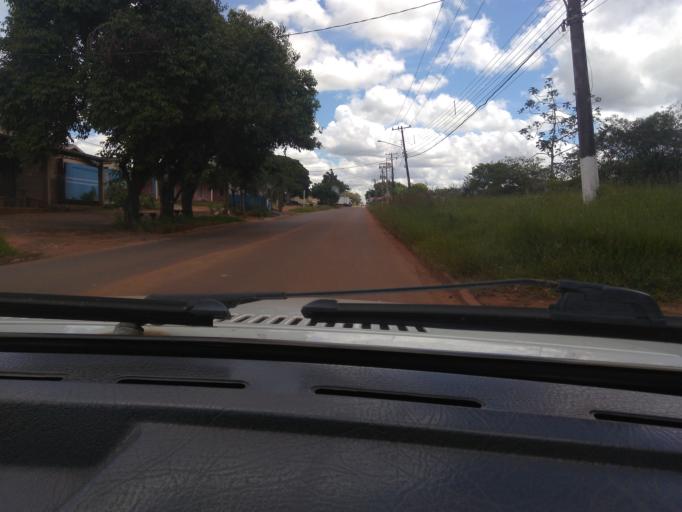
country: BR
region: Mato Grosso do Sul
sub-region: Ponta Pora
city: Ponta Pora
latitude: -22.5062
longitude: -55.7278
